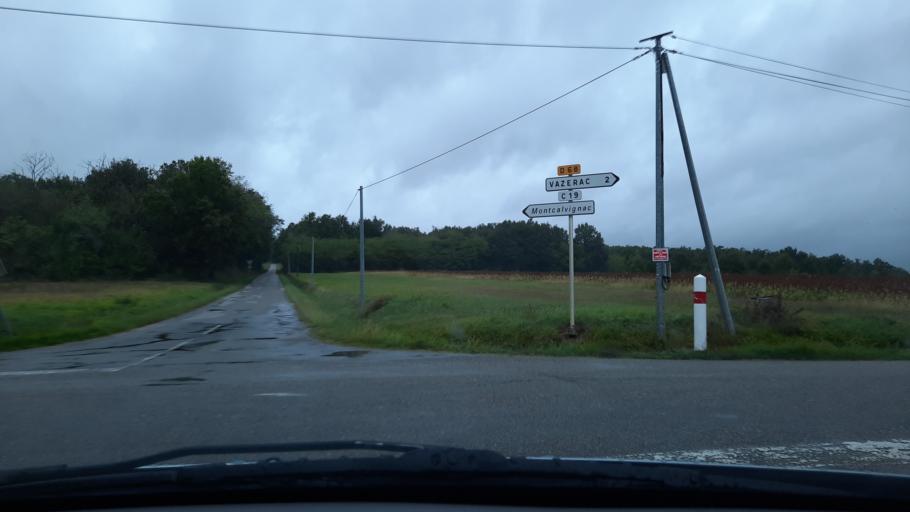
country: FR
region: Midi-Pyrenees
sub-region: Departement du Tarn-et-Garonne
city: Lafrancaise
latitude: 44.1784
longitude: 1.2692
